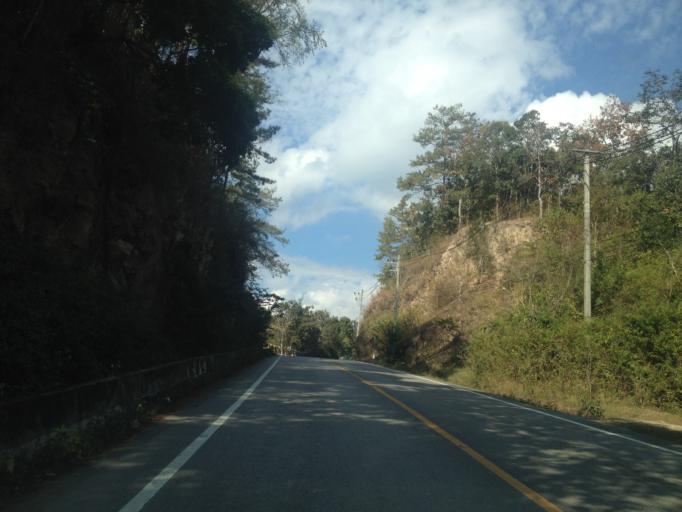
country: TH
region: Mae Hong Son
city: Ban Huai I Huak
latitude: 18.1406
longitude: 98.1718
